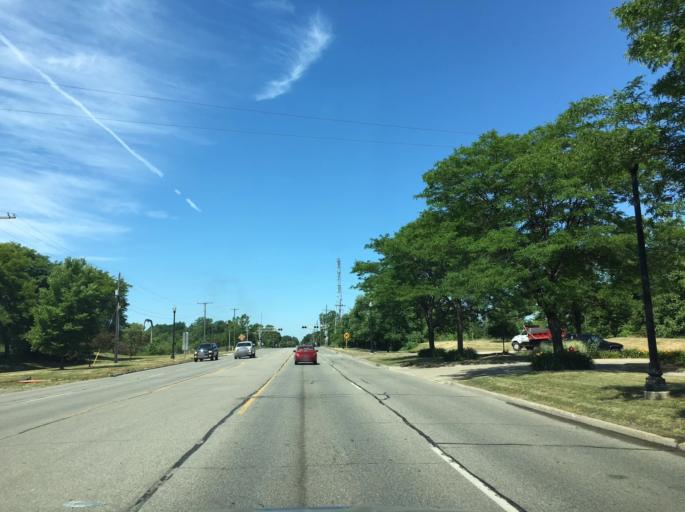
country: US
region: Michigan
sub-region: Wayne County
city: Allen Park
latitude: 42.2276
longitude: -83.2322
